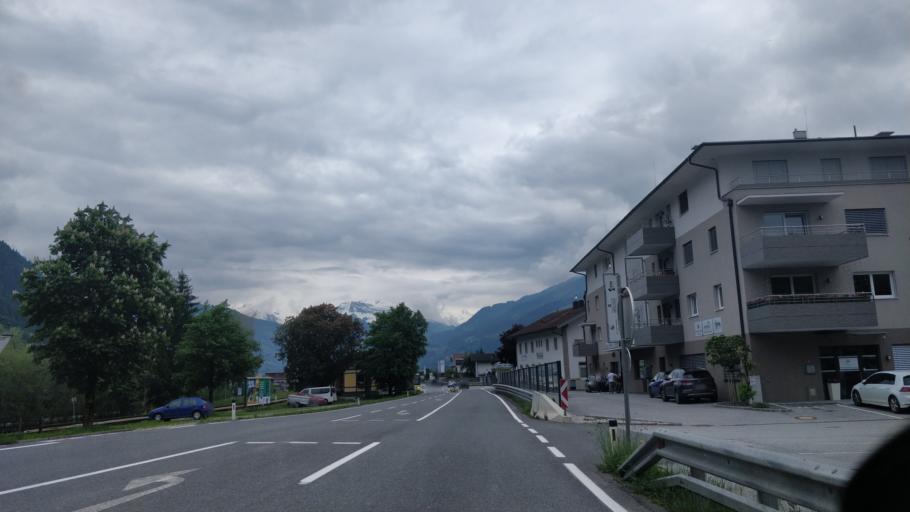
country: AT
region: Tyrol
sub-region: Politischer Bezirk Schwaz
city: Uderns
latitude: 47.3274
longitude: 11.8646
